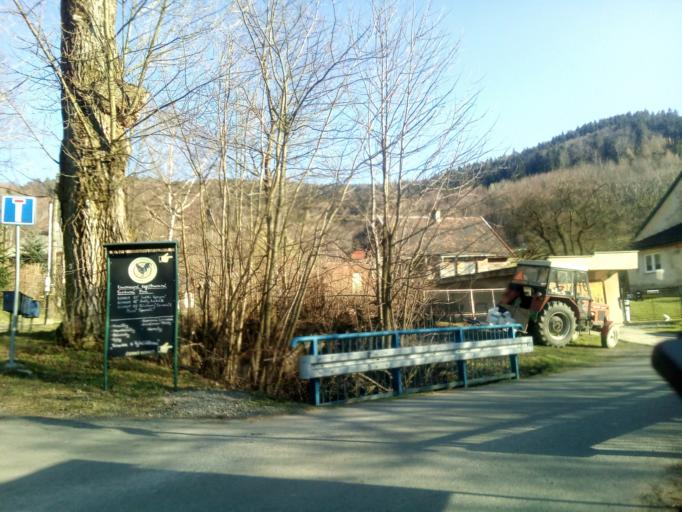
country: CZ
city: Dobratice
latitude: 49.6436
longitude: 18.4811
